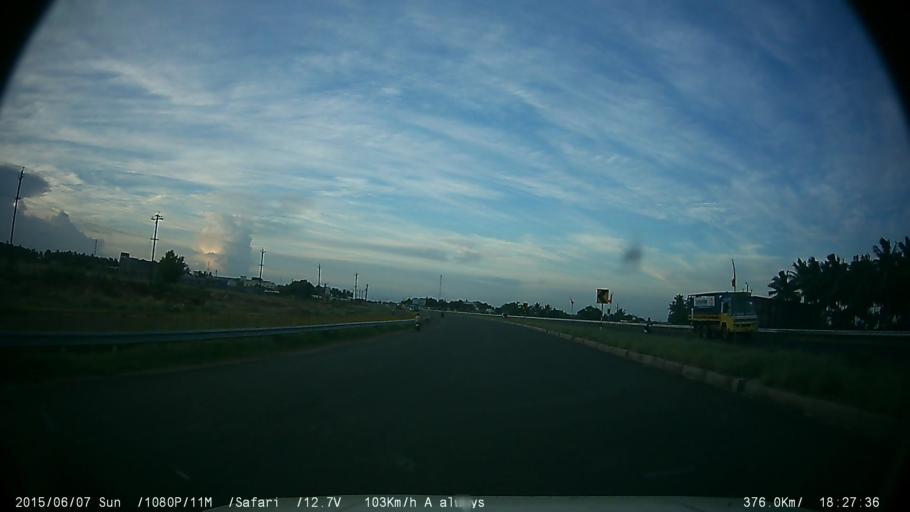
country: IN
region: Tamil Nadu
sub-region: Tiruppur
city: Avinashi
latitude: 11.1370
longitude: 77.2026
